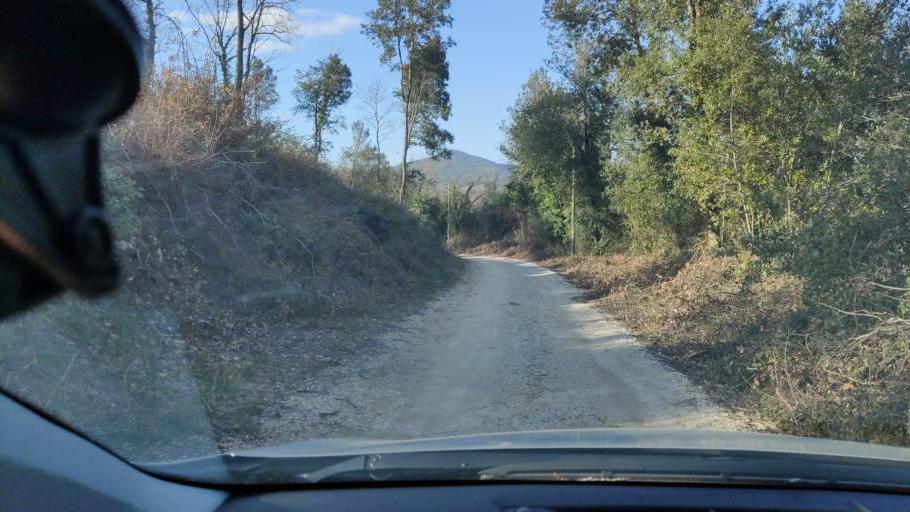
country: IT
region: Umbria
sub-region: Provincia di Terni
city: Amelia
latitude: 42.5631
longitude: 12.4410
